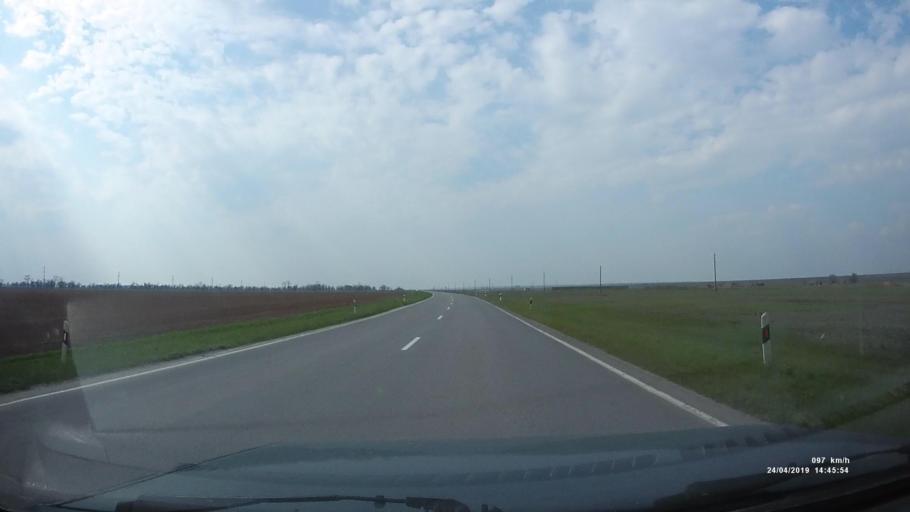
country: RU
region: Rostov
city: Remontnoye
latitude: 46.4769
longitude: 43.7991
